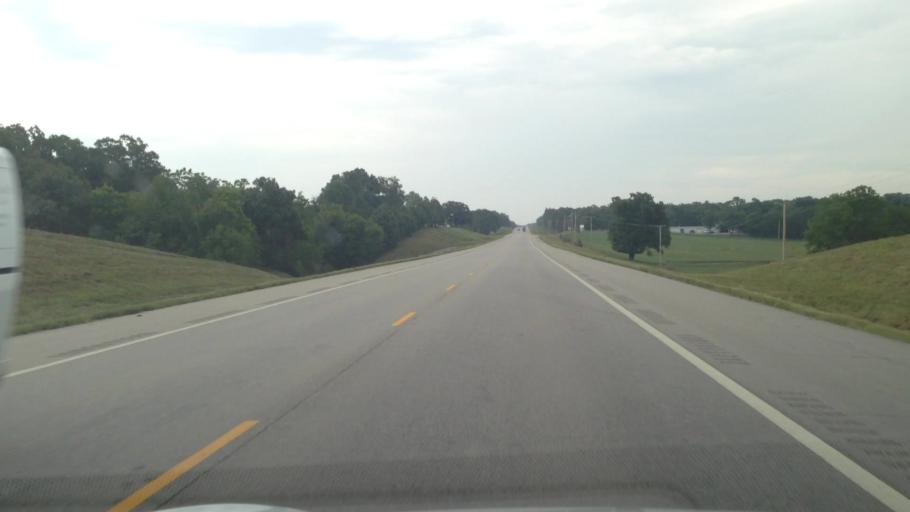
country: US
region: Kansas
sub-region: Cherokee County
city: Galena
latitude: 37.0236
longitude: -94.6732
